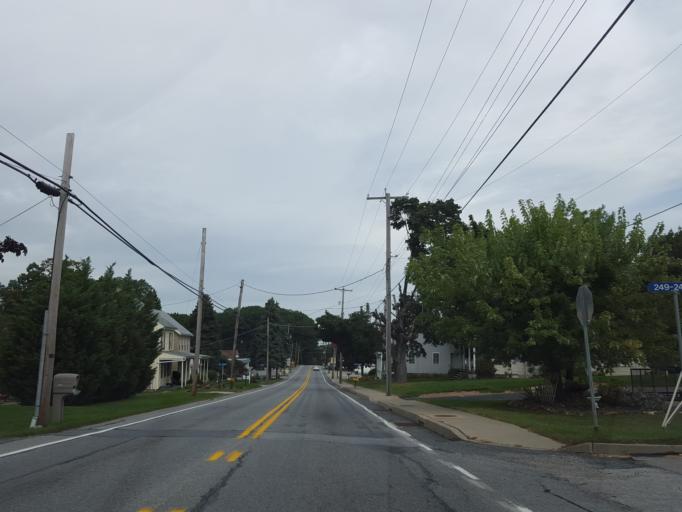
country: US
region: Pennsylvania
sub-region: York County
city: West York
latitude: 39.9068
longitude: -76.7906
